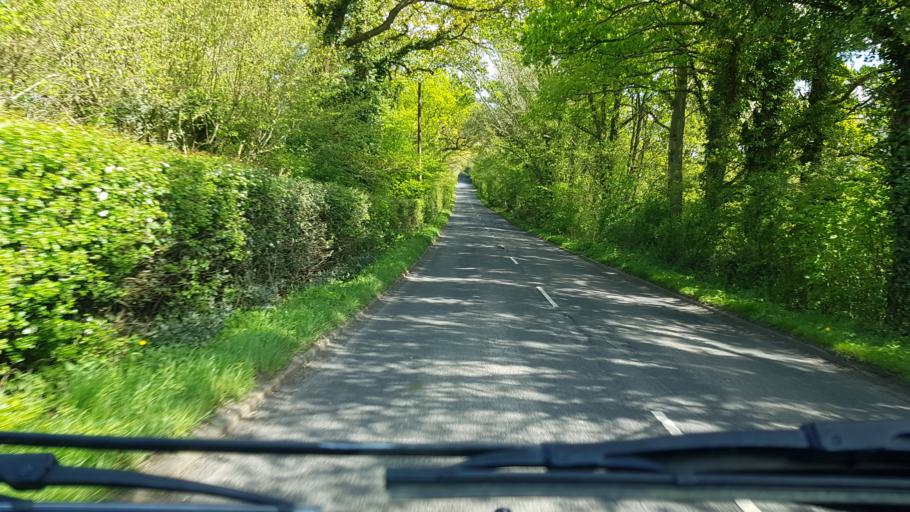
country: GB
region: England
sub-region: East Sussex
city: Robertsbridge
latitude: 51.0317
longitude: 0.4463
